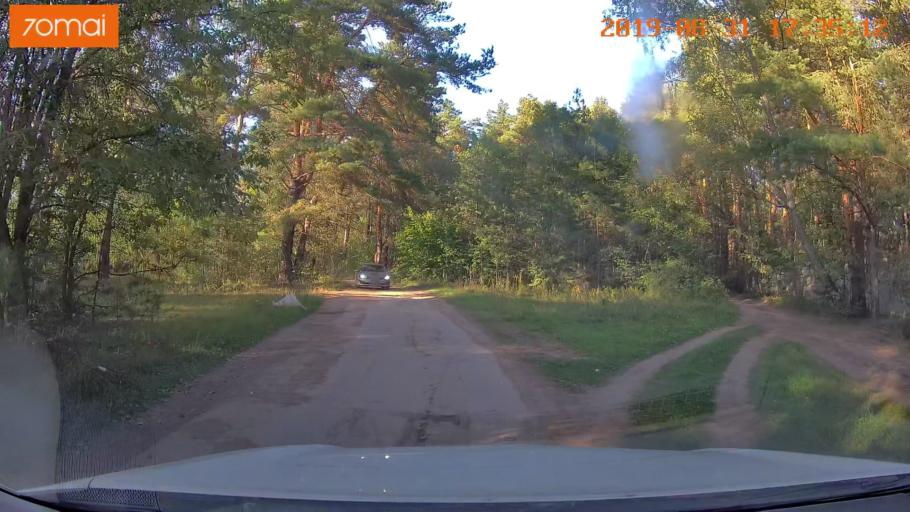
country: RU
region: Kaluga
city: Detchino
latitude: 54.8149
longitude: 36.3531
